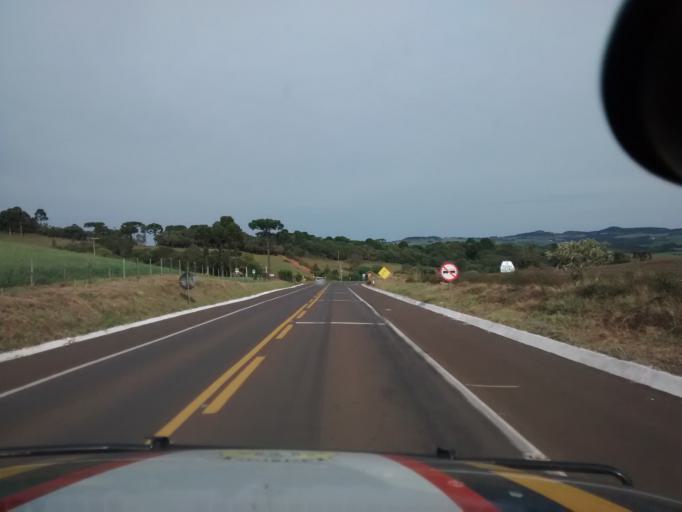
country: BR
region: Rio Grande do Sul
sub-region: Lagoa Vermelha
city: Lagoa Vermelha
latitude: -28.3364
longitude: -51.3042
